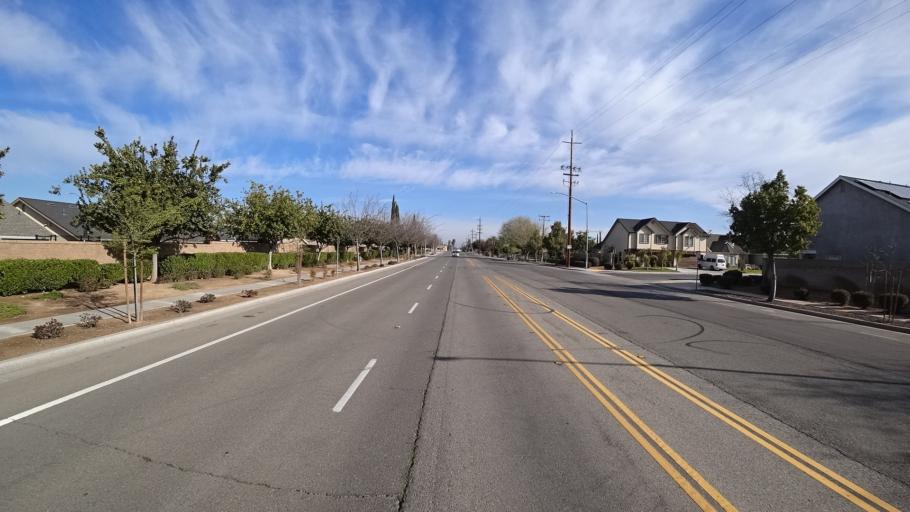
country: US
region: California
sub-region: Fresno County
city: West Park
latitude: 36.7765
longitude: -119.8804
